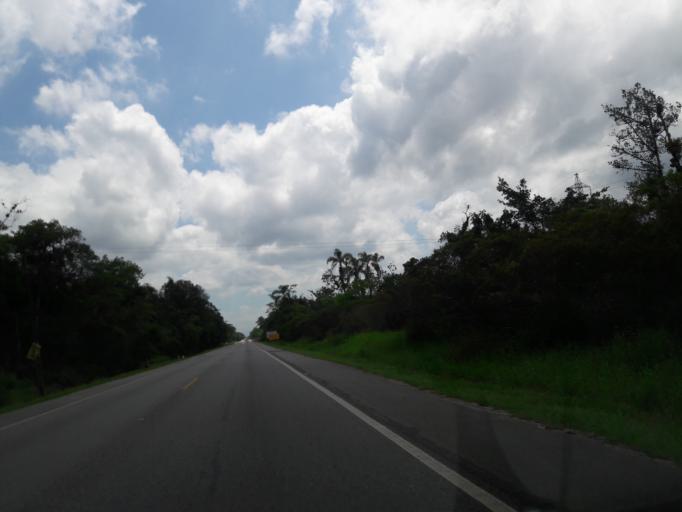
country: BR
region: Parana
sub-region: Pontal Do Parana
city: Pontal do Parana
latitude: -25.6458
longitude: -48.5302
